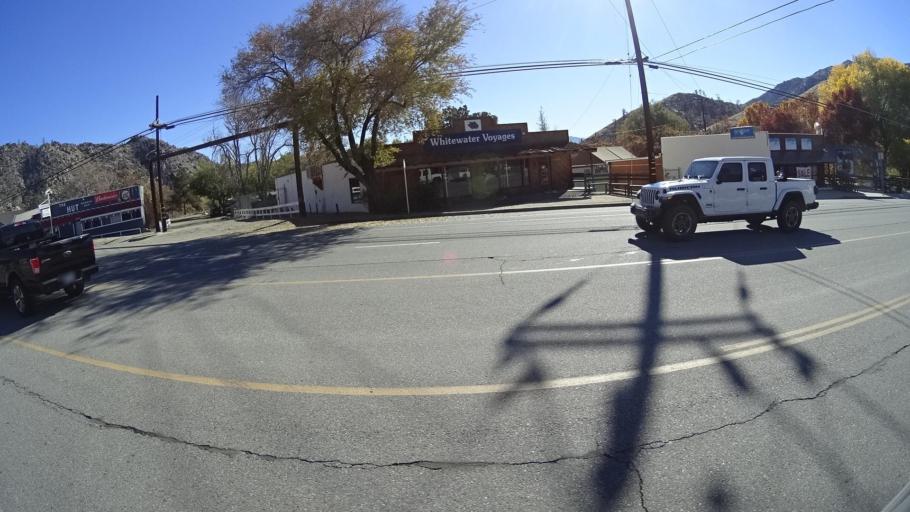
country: US
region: California
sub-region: Kern County
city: Kernville
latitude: 35.7552
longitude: -118.4211
